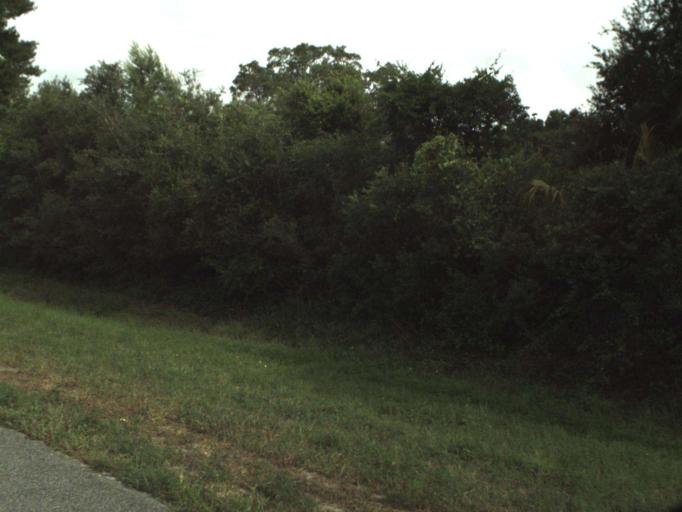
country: US
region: Florida
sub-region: Seminole County
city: Geneva
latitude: 28.7248
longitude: -81.0952
